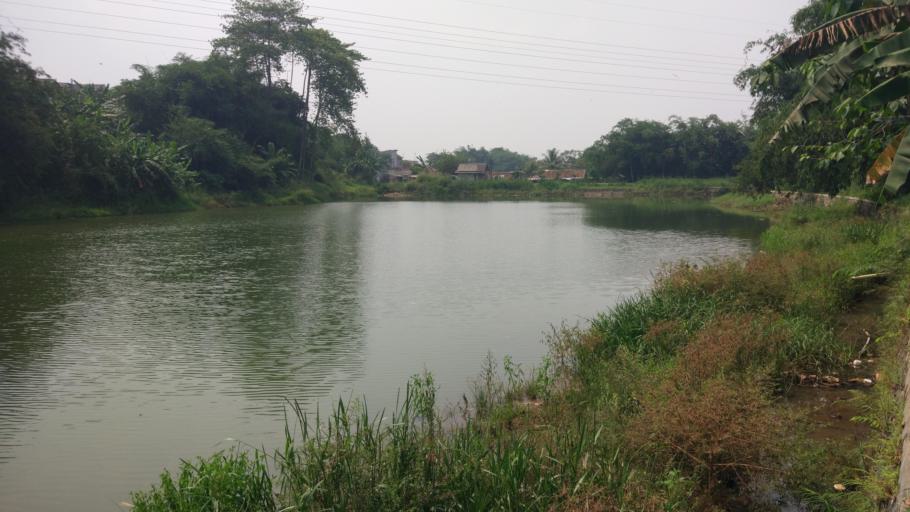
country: ID
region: West Java
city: Ciampea
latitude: -6.5816
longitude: 106.7339
